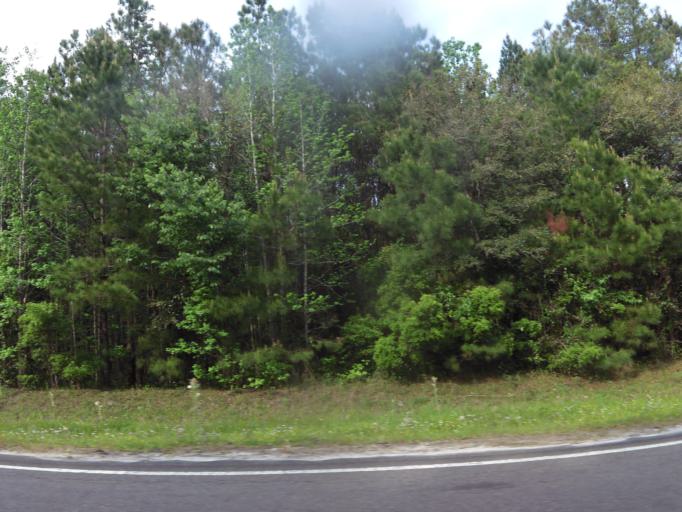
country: US
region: Georgia
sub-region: Camden County
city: Kingsland
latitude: 30.6982
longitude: -81.7451
